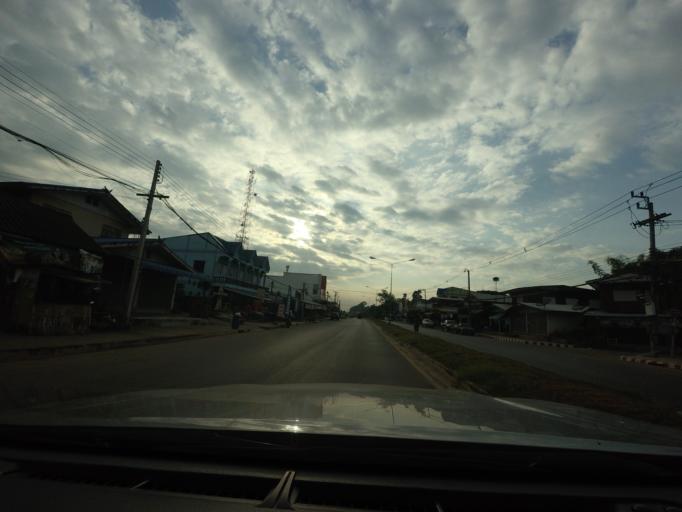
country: TH
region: Phitsanulok
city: Noen Maprang
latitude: 16.5685
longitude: 100.6394
